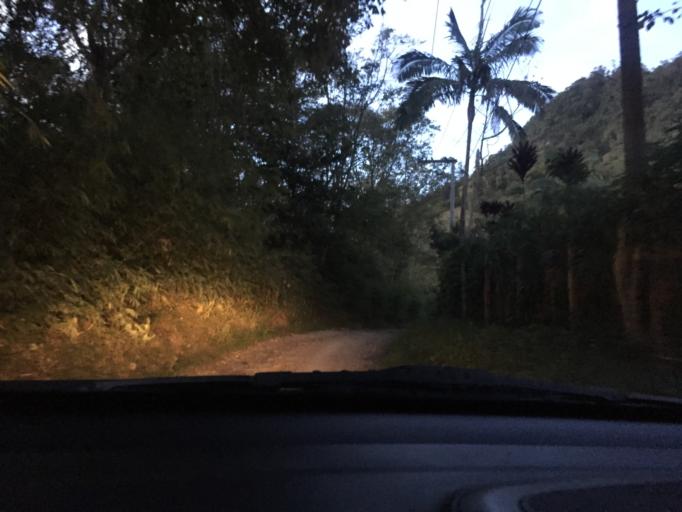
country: CO
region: Cundinamarca
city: Zipacon
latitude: 4.7196
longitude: -74.4152
